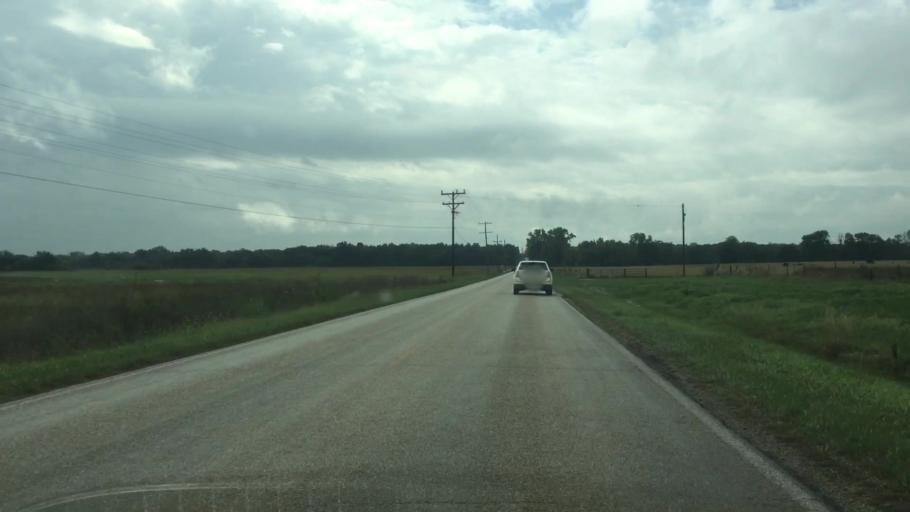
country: US
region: Kansas
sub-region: Allen County
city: Iola
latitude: 37.8756
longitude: -95.4369
